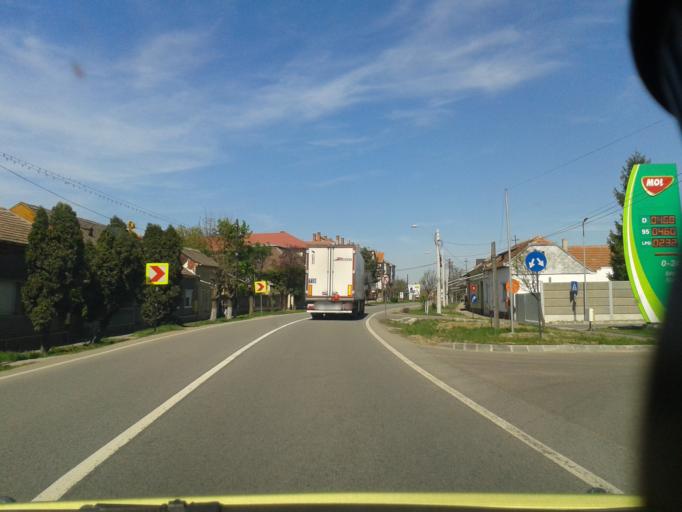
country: RO
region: Bihor
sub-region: Municipiul Salonta
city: Salonta
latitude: 46.8072
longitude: 21.6609
